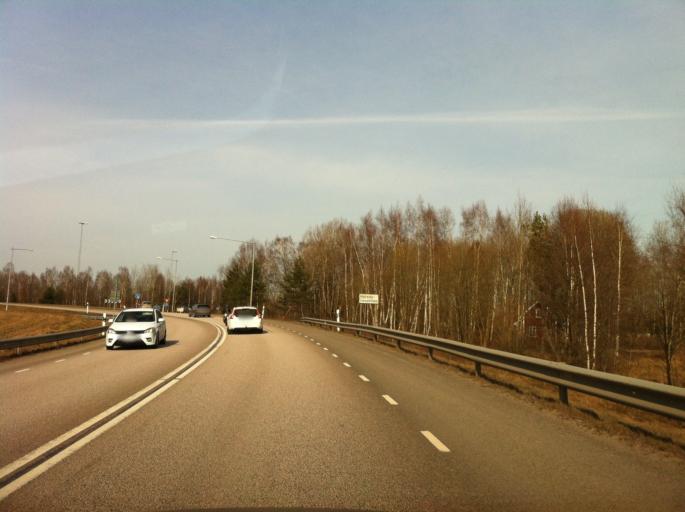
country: SE
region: Vaestra Goetaland
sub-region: Skovde Kommun
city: Skoevde
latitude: 58.4183
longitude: 13.8859
